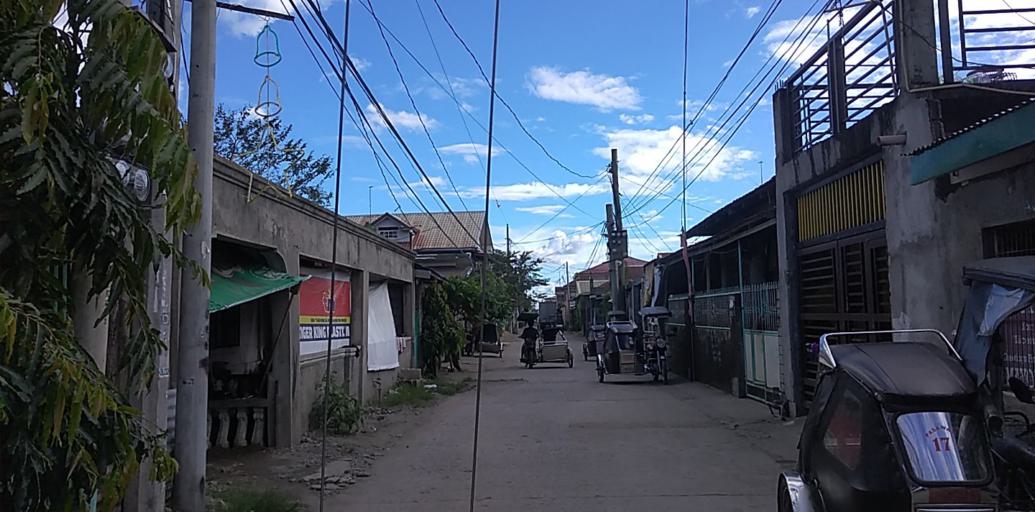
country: PH
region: Central Luzon
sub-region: Province of Pampanga
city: Arayat
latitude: 15.1420
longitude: 120.7687
